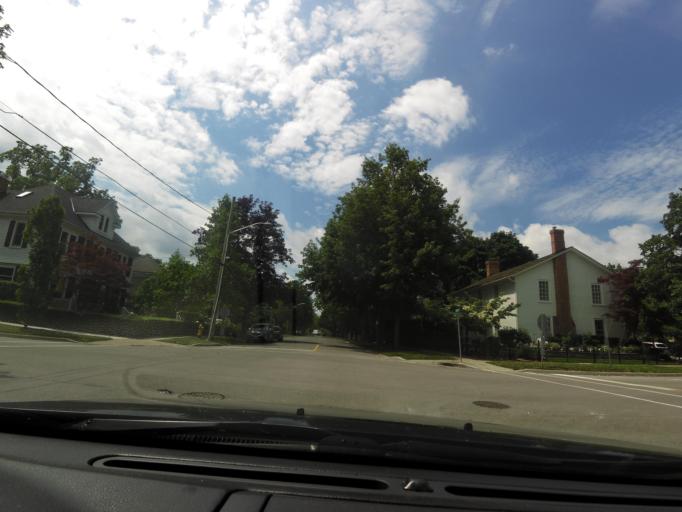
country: US
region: New York
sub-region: Niagara County
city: Youngstown
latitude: 43.2583
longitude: -79.0743
